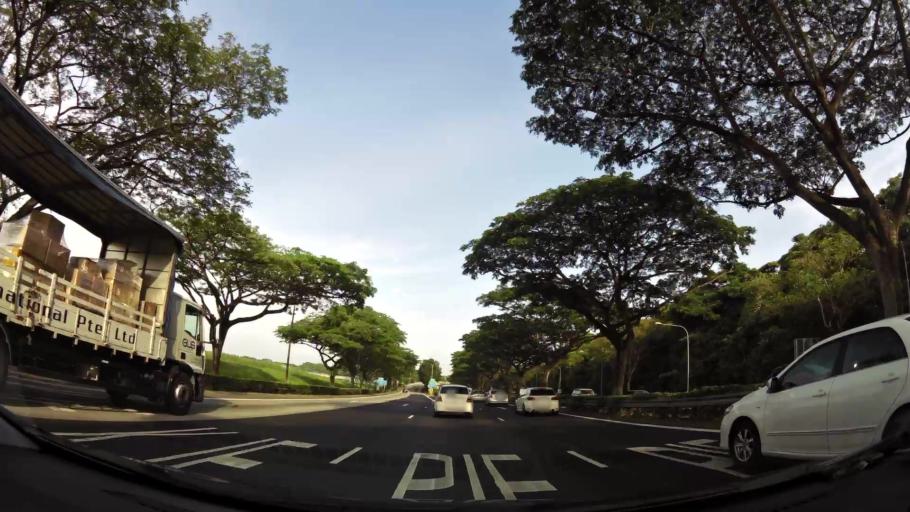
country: MY
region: Johor
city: Johor Bahru
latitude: 1.3594
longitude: 103.7117
